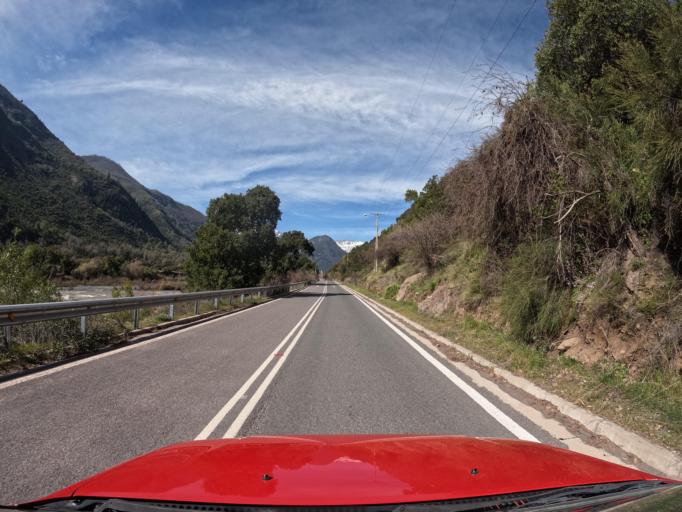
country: CL
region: O'Higgins
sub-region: Provincia de Colchagua
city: Chimbarongo
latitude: -35.0006
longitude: -70.7980
